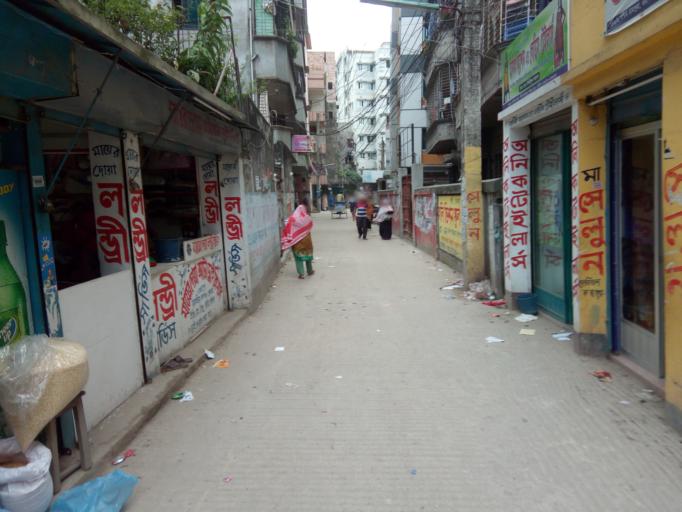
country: BD
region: Dhaka
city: Paltan
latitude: 23.7618
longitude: 90.4159
